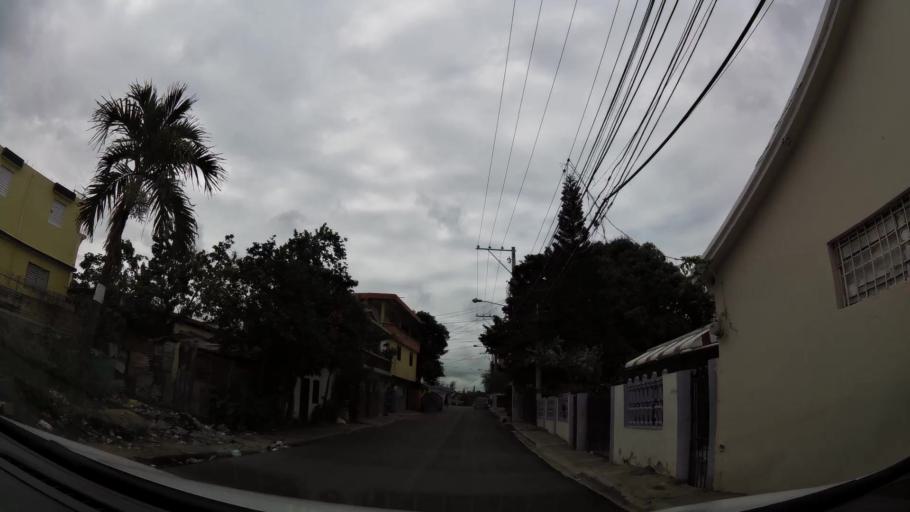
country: DO
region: Santiago
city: Santiago de los Caballeros
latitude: 19.4294
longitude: -70.6690
